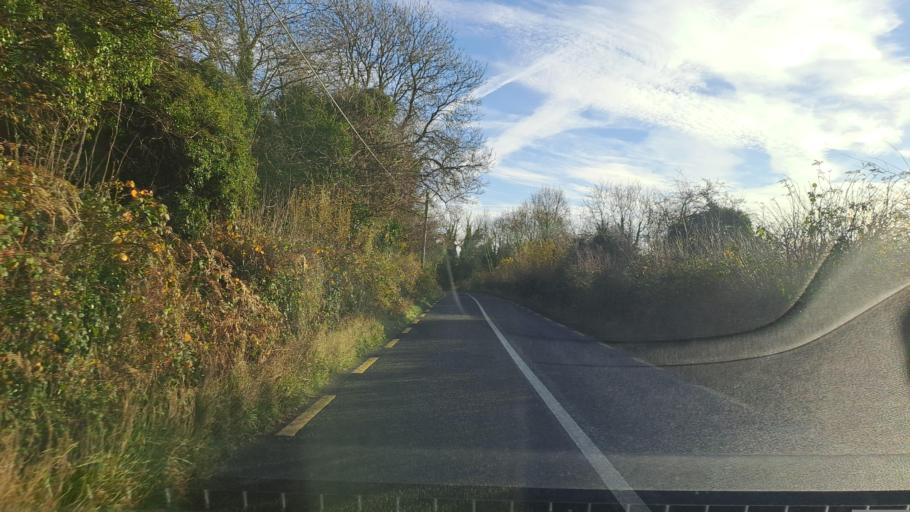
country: IE
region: Ulster
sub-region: County Monaghan
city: Carrickmacross
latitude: 53.8729
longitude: -6.7109
